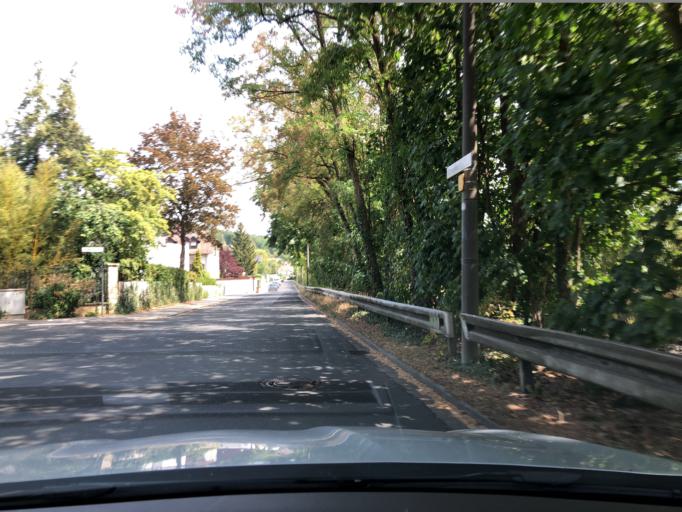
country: DE
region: Bavaria
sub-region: Regierungsbezirk Mittelfranken
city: Ruckersdorf
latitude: 49.4979
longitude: 11.2457
